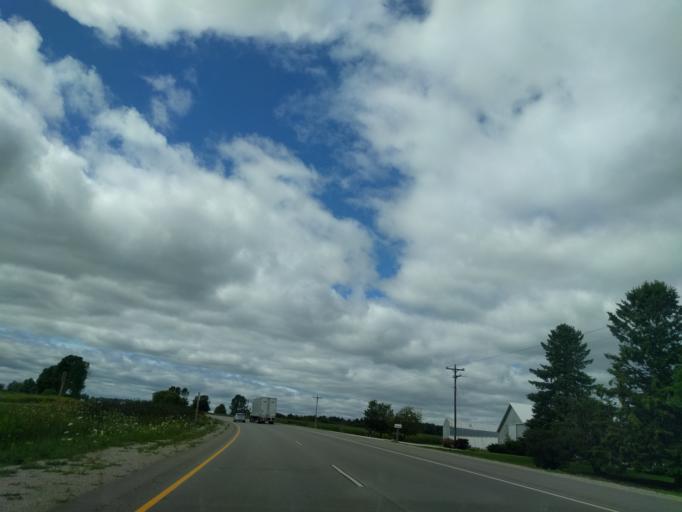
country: US
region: Wisconsin
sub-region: Oconto County
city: Oconto Falls
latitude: 44.8002
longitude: -88.0186
